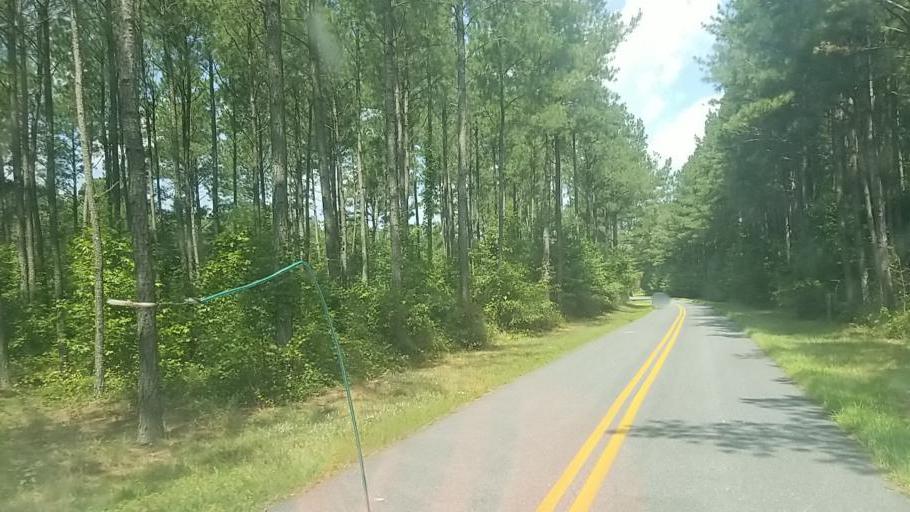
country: US
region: Maryland
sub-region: Worcester County
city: Snow Hill
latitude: 38.2755
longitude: -75.4733
